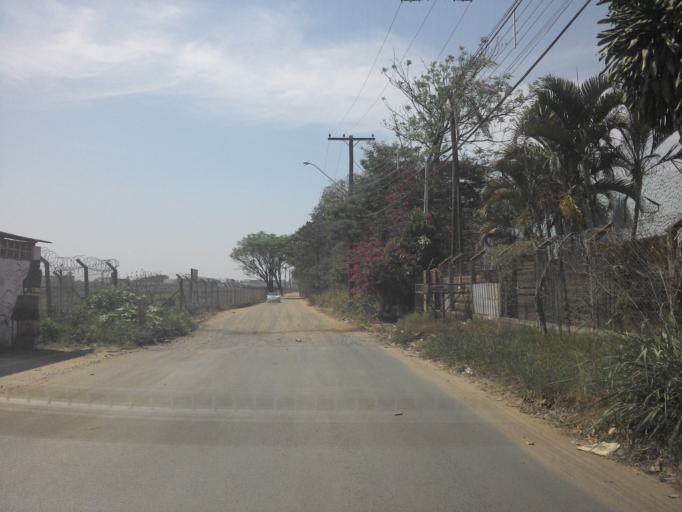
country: BR
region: Sao Paulo
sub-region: Hortolandia
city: Hortolandia
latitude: -22.9125
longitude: -47.2065
